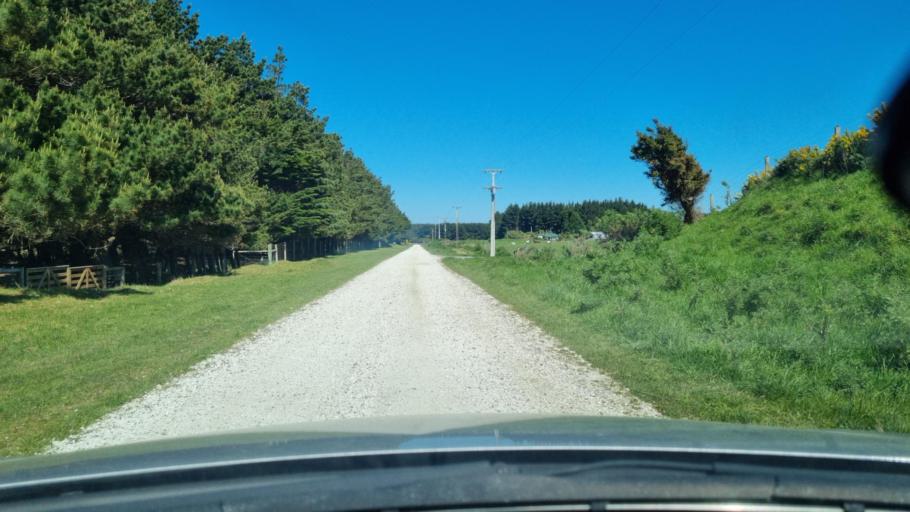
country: NZ
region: Southland
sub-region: Invercargill City
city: Invercargill
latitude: -46.4556
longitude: 168.2743
